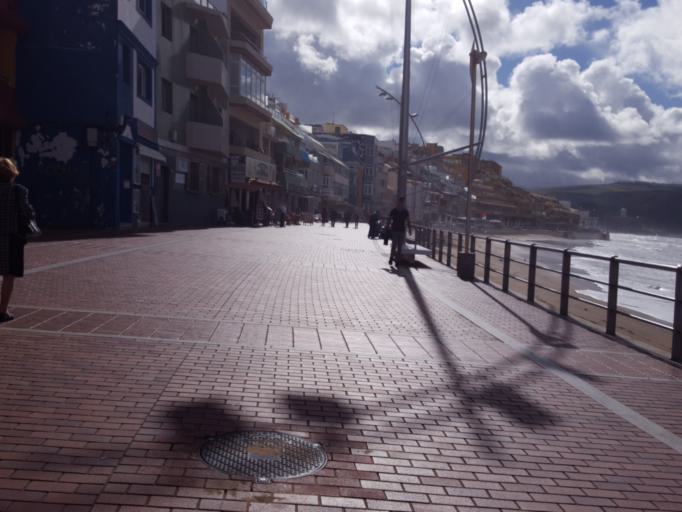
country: ES
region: Canary Islands
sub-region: Provincia de Las Palmas
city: Las Palmas de Gran Canaria
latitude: 28.1379
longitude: -15.4370
